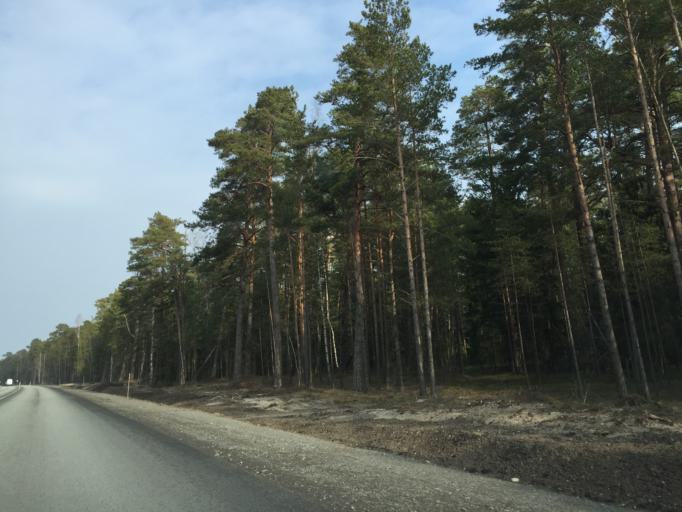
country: LV
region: Salacgrivas
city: Ainazi
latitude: 57.8176
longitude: 24.3472
